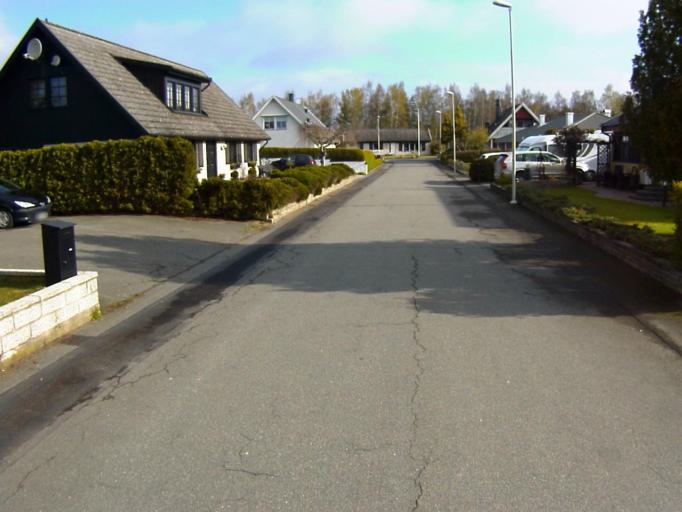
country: SE
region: Skane
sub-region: Kristianstads Kommun
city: Kristianstad
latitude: 56.0150
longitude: 14.1076
